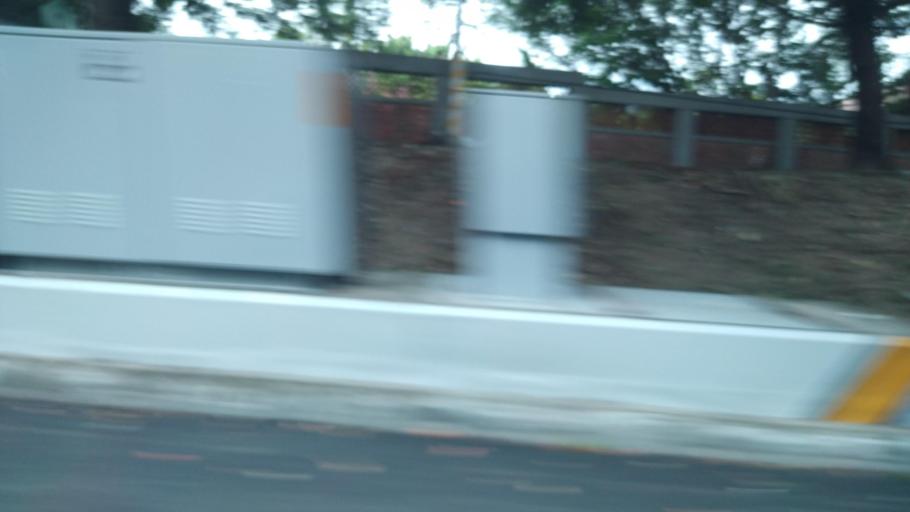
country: TW
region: Taiwan
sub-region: Hualien
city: Hualian
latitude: 24.0005
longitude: 121.6202
